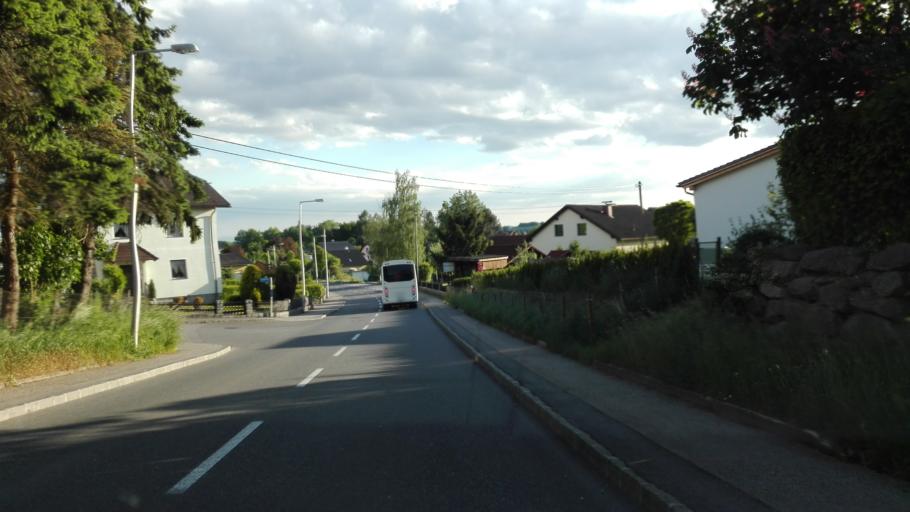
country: AT
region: Upper Austria
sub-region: Politischer Bezirk Urfahr-Umgebung
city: Engerwitzdorf
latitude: 48.3631
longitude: 14.5350
